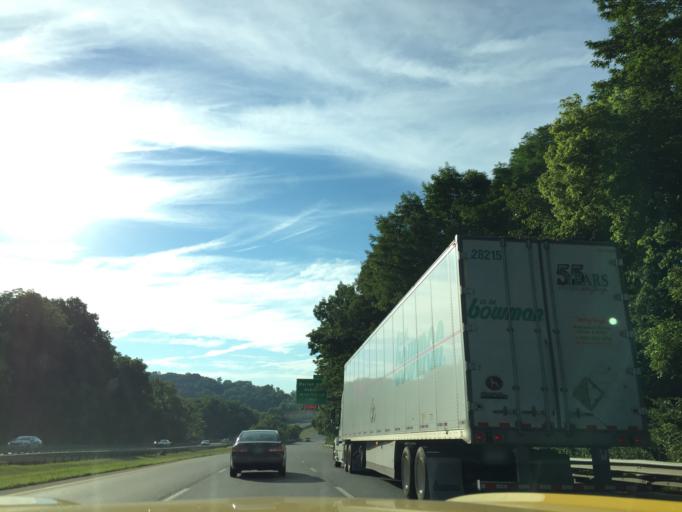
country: US
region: New Jersey
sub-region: Warren County
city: Alpha
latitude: 40.6718
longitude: -75.1093
